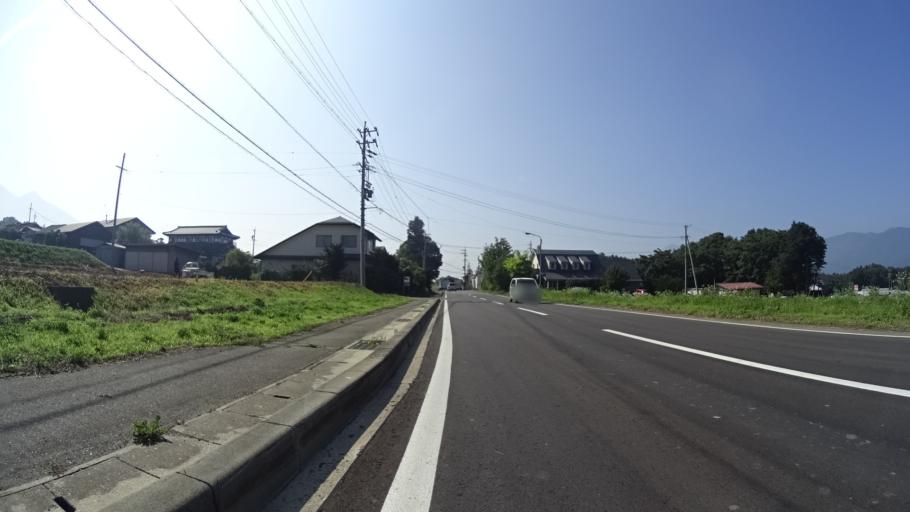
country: JP
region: Nagano
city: Chino
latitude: 35.9459
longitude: 138.2429
